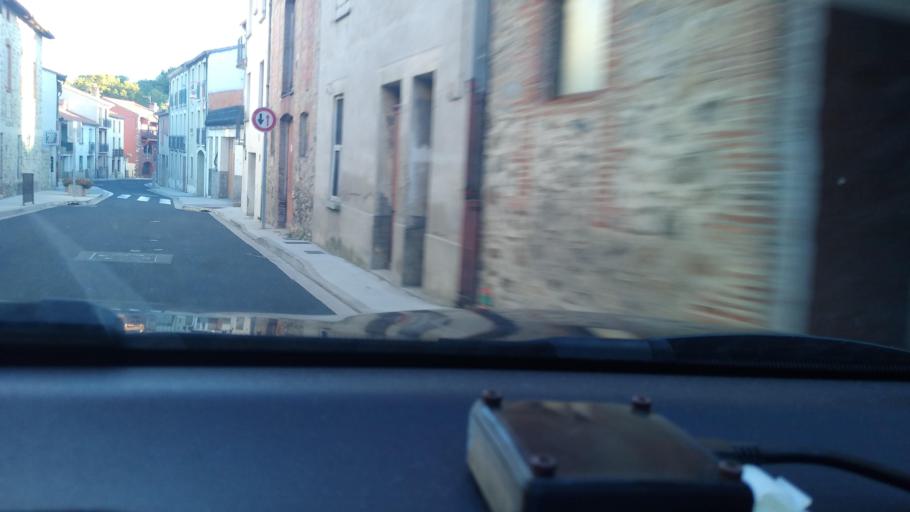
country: FR
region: Languedoc-Roussillon
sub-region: Departement des Pyrenees-Orientales
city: Prades
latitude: 42.6339
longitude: 2.4209
